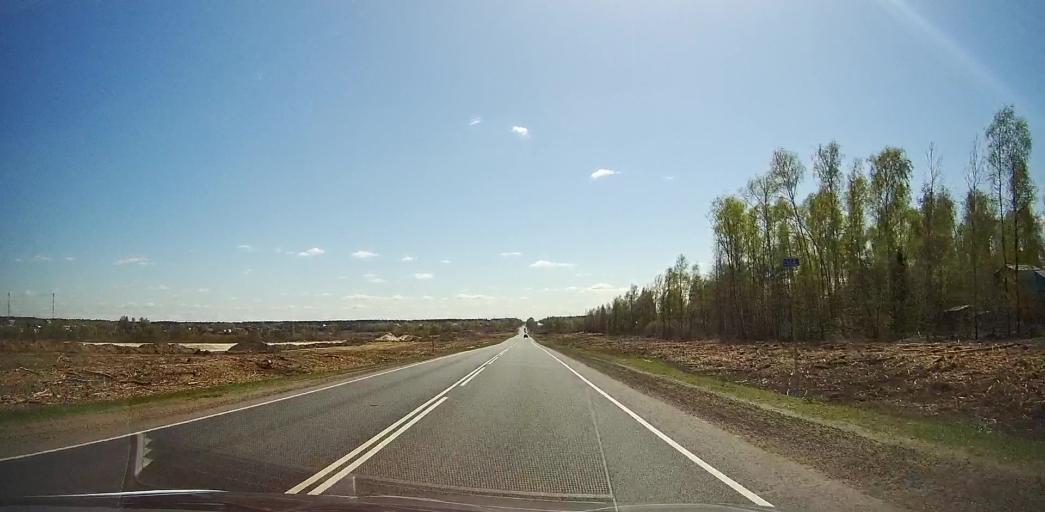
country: RU
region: Moskovskaya
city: Gzhel'
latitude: 55.5841
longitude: 38.3858
